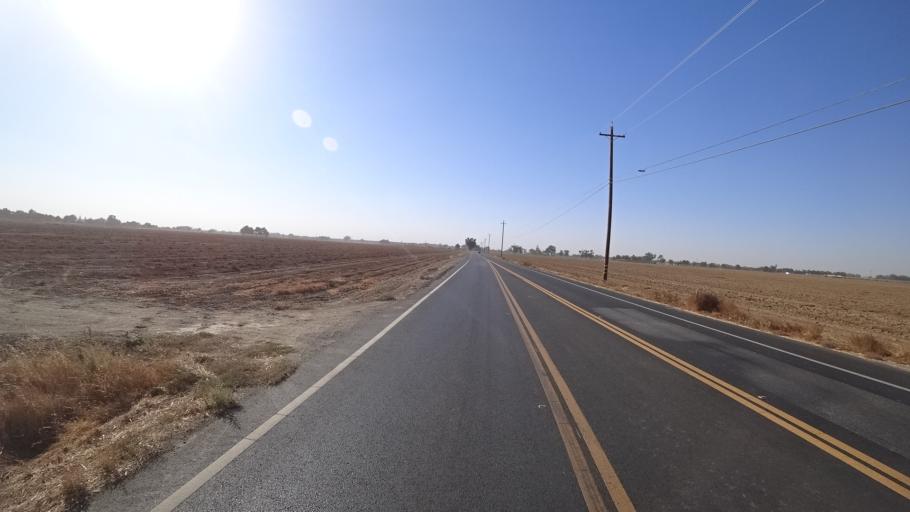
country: US
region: California
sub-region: Yolo County
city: Woodland
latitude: 38.7351
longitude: -121.7663
